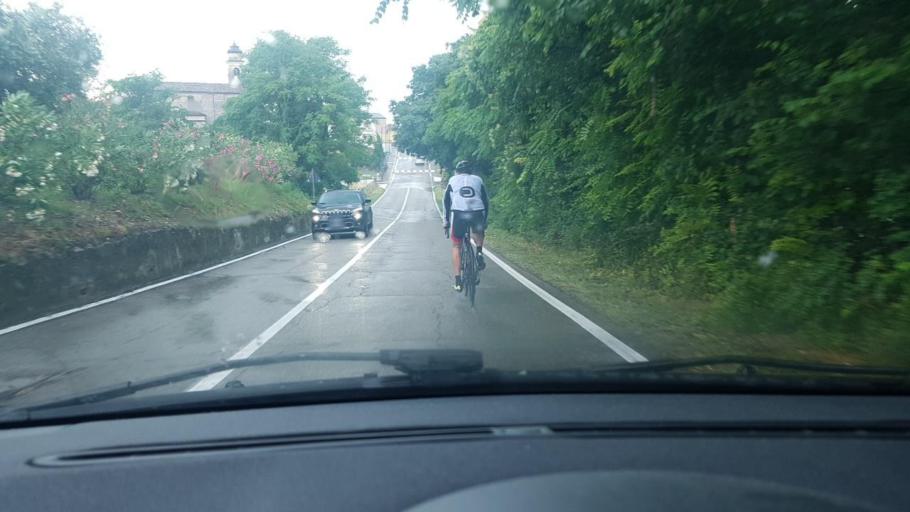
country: IT
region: Veneto
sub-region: Provincia di Verona
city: Garda
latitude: 45.5937
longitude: 10.7124
